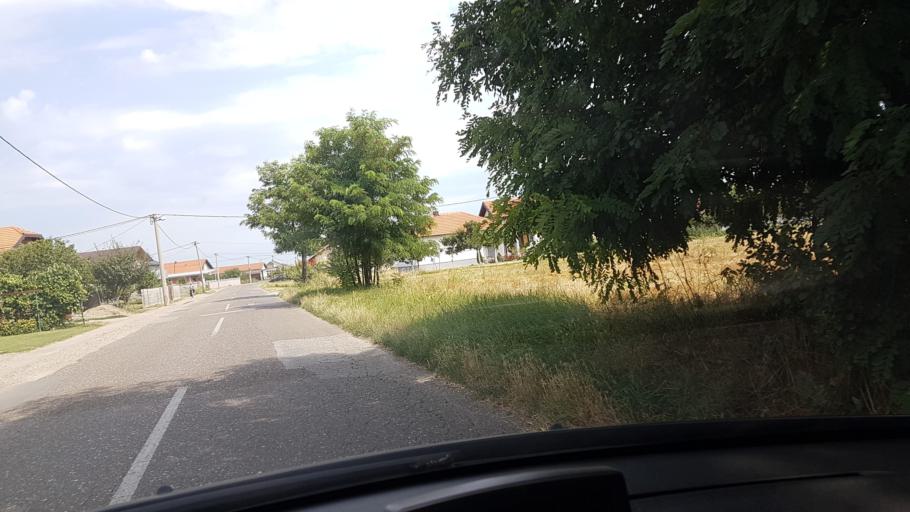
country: BA
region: Republika Srpska
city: Bijeljina
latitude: 44.7857
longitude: 19.2225
